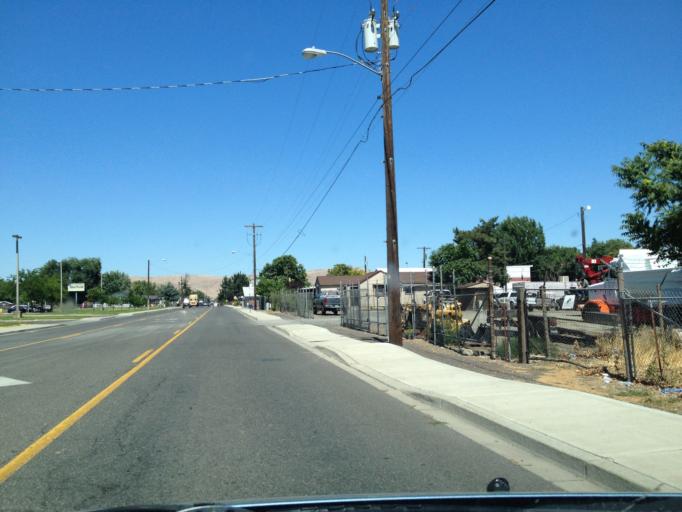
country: US
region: Washington
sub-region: Yakima County
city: Union Gap
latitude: 46.5720
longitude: -120.4779
